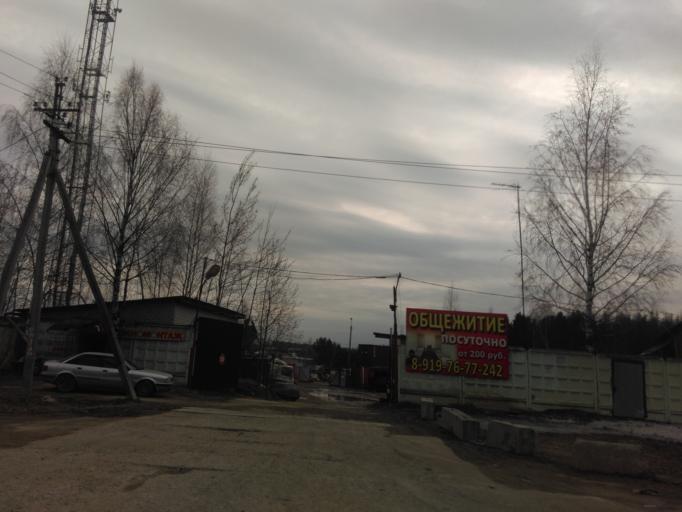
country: RU
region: Moskovskaya
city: Tuchkovo
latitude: 55.6022
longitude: 36.4483
